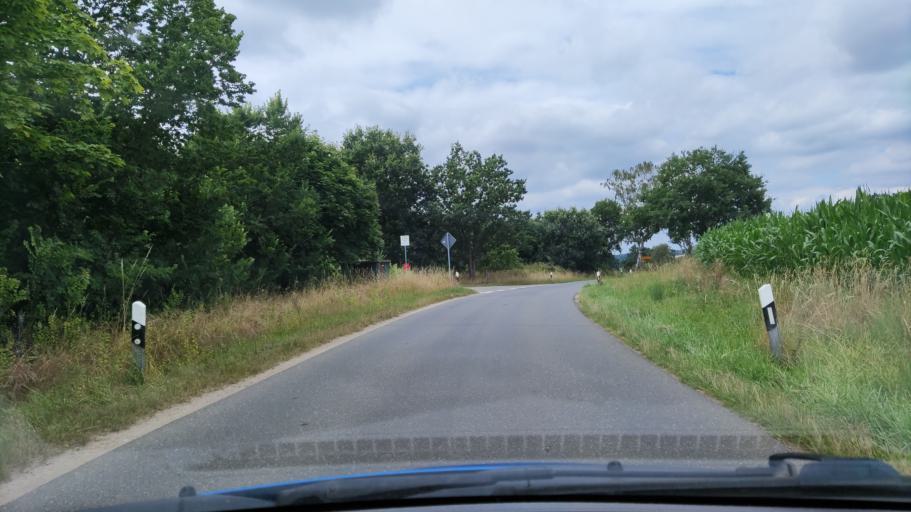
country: DE
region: Lower Saxony
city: Weste
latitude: 53.0686
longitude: 10.6930
